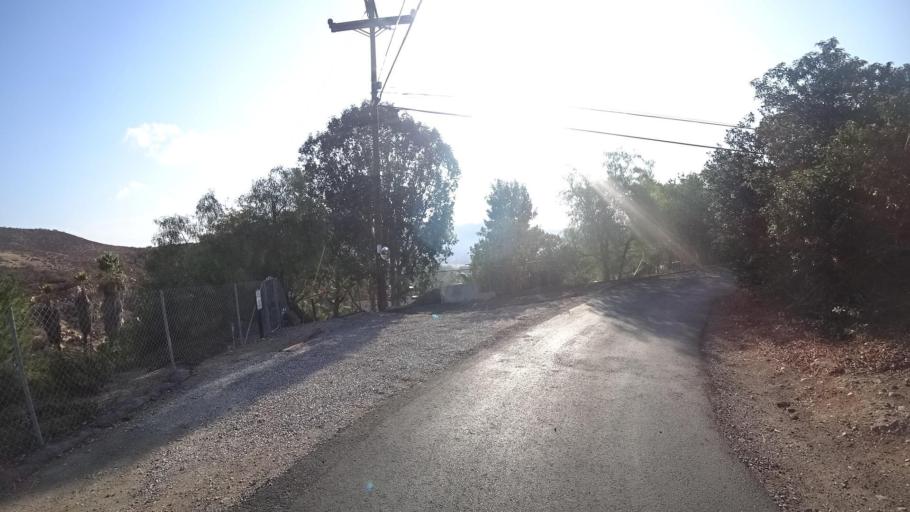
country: US
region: California
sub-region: San Diego County
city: Eucalyptus Hills
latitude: 32.8981
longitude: -116.9498
